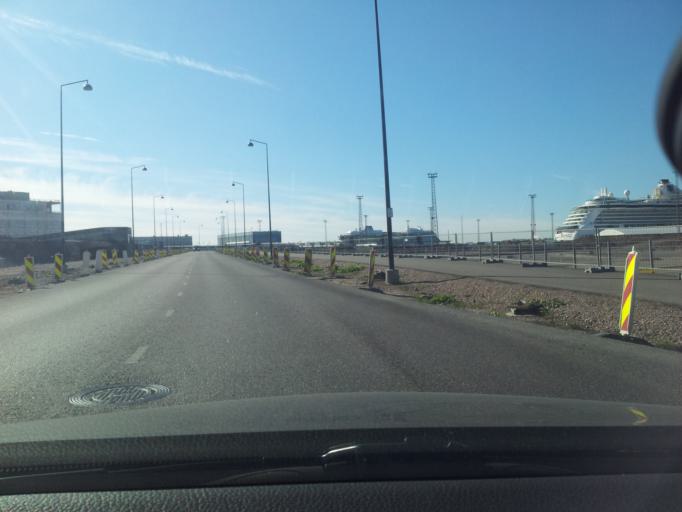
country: FI
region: Uusimaa
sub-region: Helsinki
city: Helsinki
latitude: 60.1569
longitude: 24.9120
